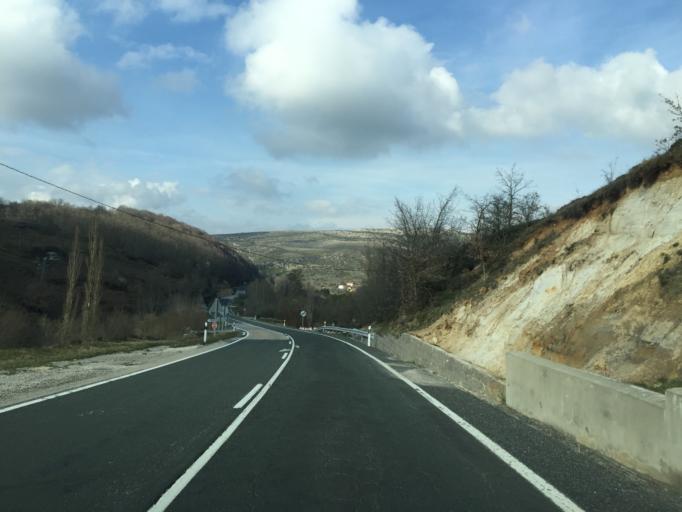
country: ES
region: Cantabria
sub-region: Provincia de Cantabria
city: San Martin de Elines
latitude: 42.9159
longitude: -3.8322
